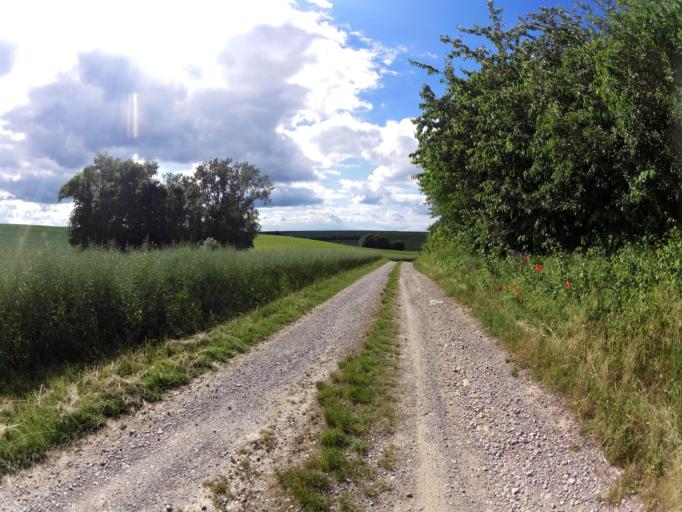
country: DE
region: Bavaria
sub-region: Regierungsbezirk Unterfranken
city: Gaukonigshofen
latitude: 49.6659
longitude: 10.0185
